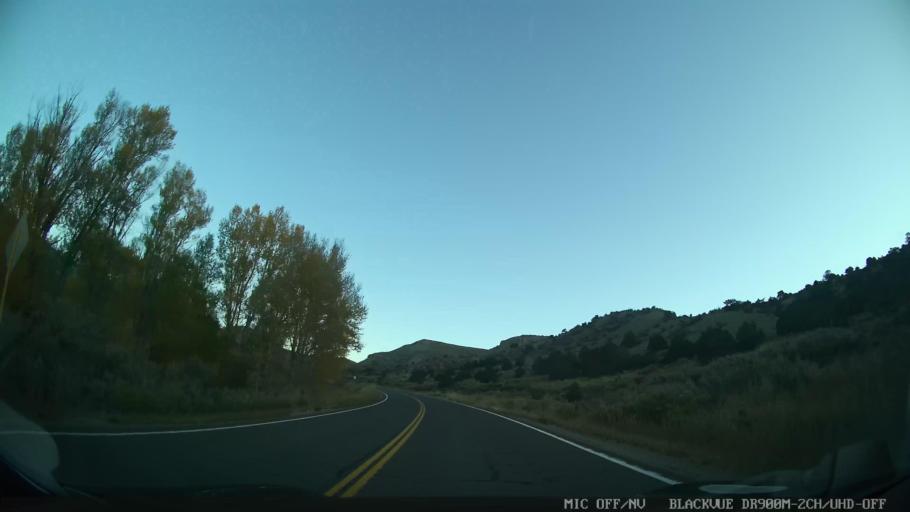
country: US
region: Colorado
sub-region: Eagle County
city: Edwards
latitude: 39.7633
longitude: -106.6775
